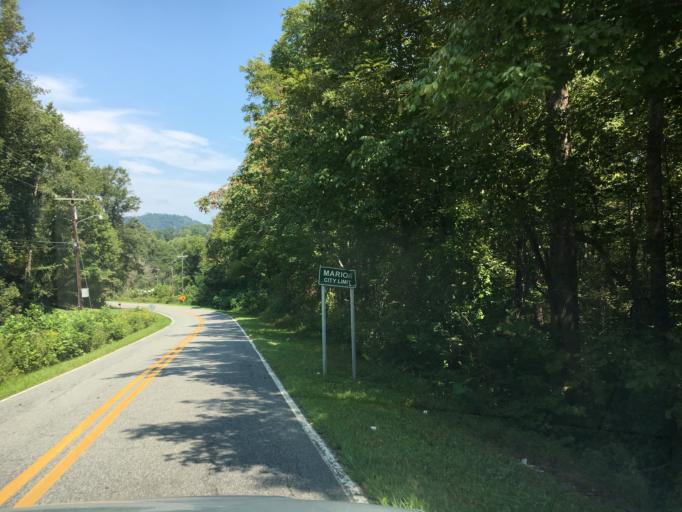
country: US
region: North Carolina
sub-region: McDowell County
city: Marion
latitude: 35.6600
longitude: -81.9742
